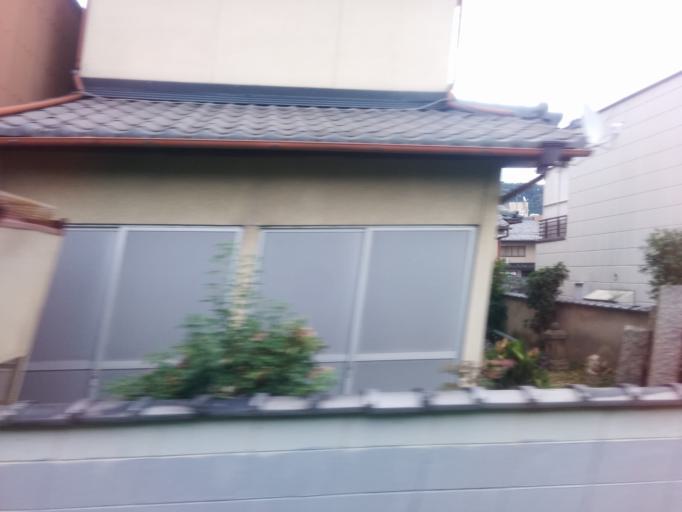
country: JP
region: Kyoto
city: Kyoto
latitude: 34.9704
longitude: 135.7704
